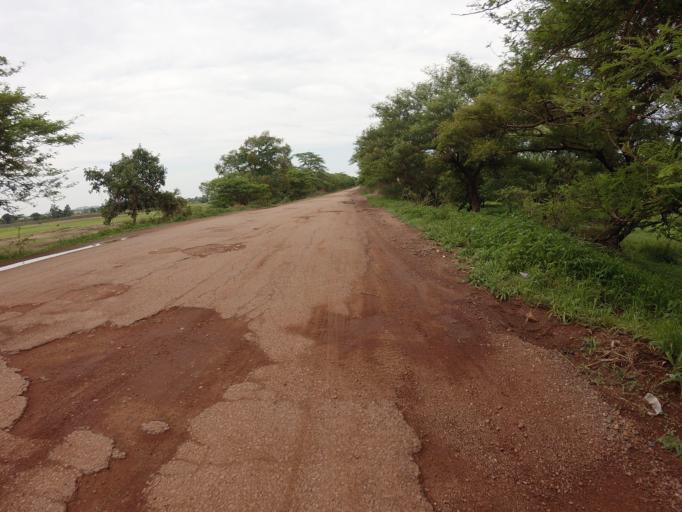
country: GH
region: Upper East
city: Bawku
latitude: 11.0028
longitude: -0.3897
